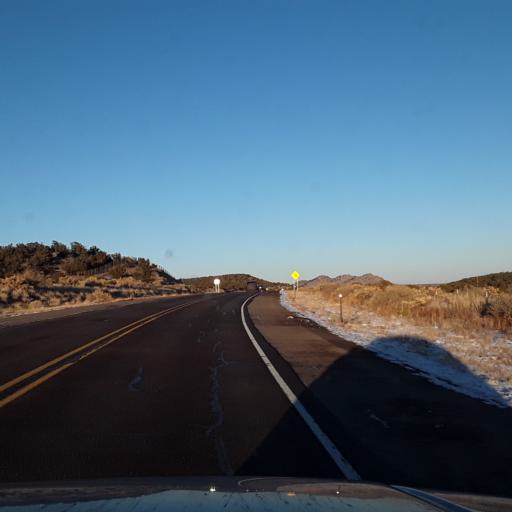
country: US
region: New Mexico
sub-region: Lincoln County
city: Carrizozo
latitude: 34.2547
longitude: -105.5931
